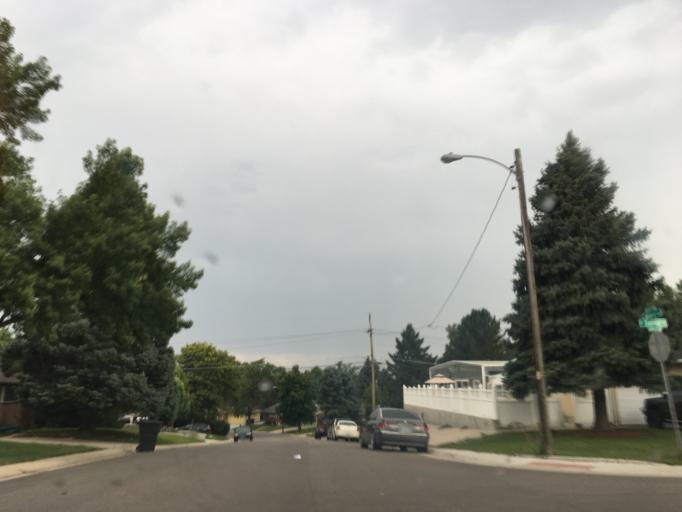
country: US
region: Colorado
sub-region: Arapahoe County
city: Sheridan
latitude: 39.6612
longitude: -105.0363
